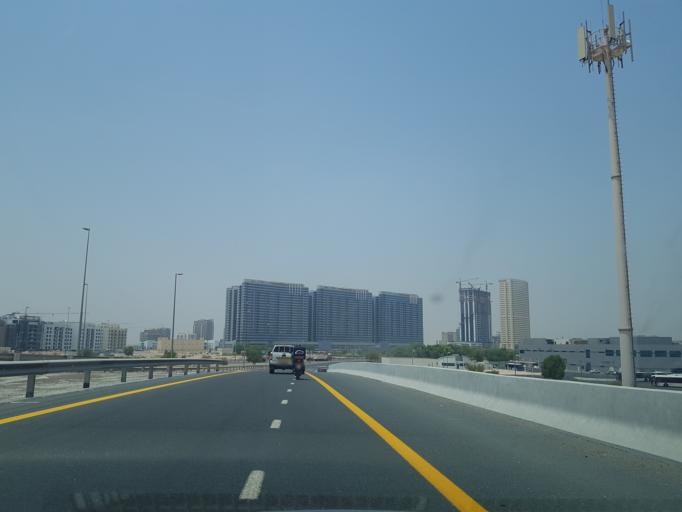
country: AE
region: Dubai
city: Dubai
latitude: 25.0897
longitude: 55.3934
